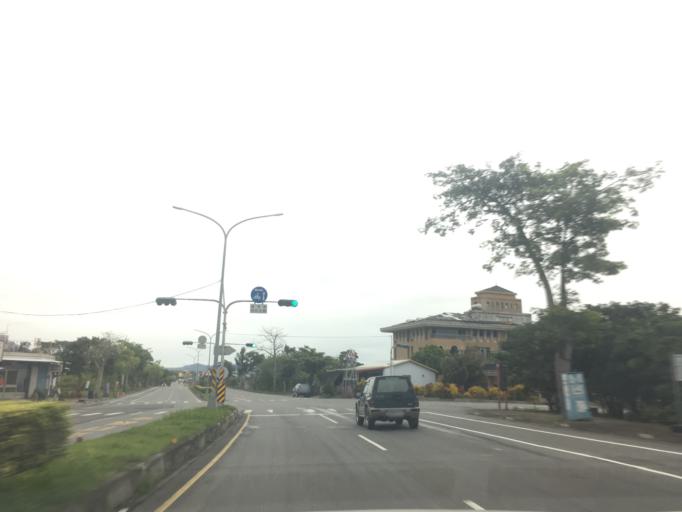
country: TW
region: Taiwan
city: Taitung City
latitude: 22.7204
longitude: 121.0534
